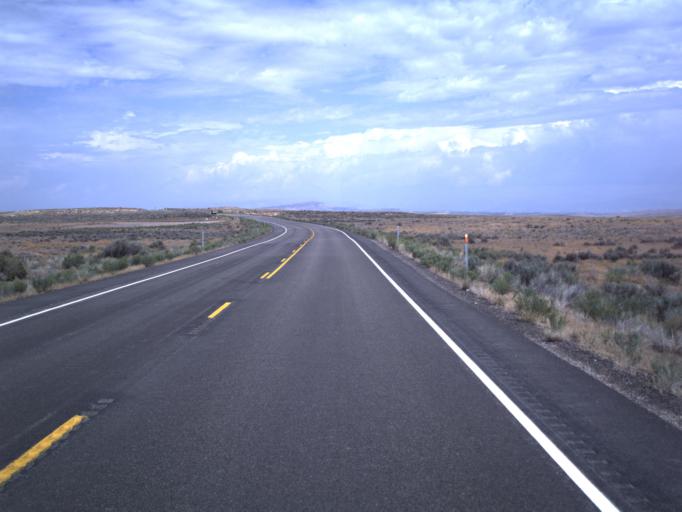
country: US
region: Utah
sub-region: Uintah County
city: Naples
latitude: 40.2464
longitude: -109.4208
